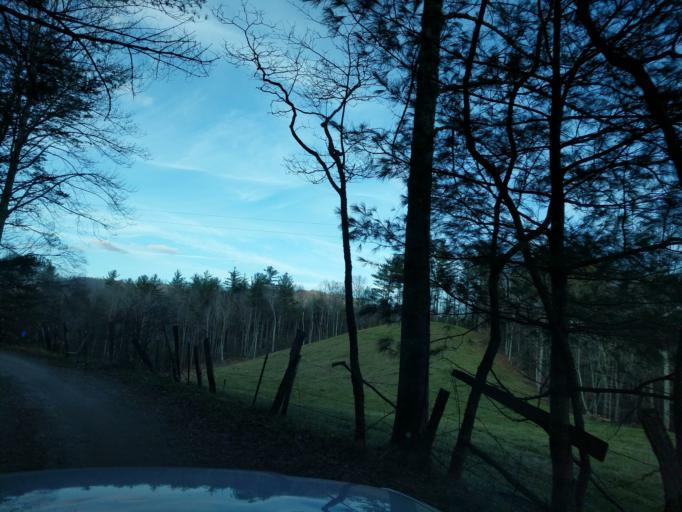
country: US
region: North Carolina
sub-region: Haywood County
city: Cove Creek
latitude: 35.7322
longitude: -83.0348
